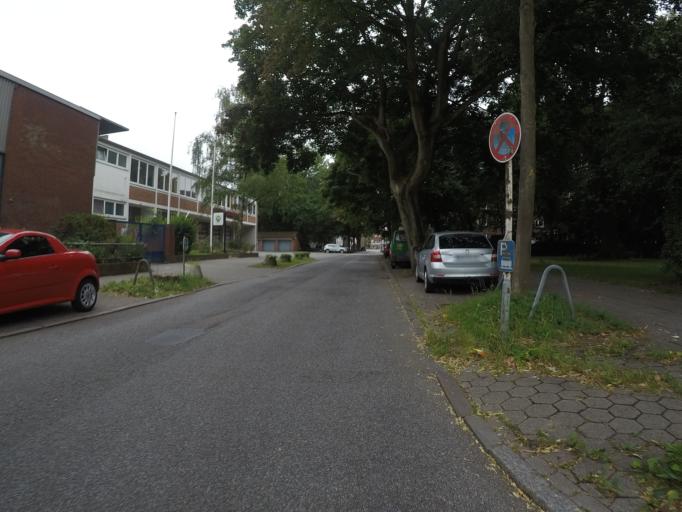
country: DE
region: Hamburg
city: Altona
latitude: 53.5350
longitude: 9.8792
